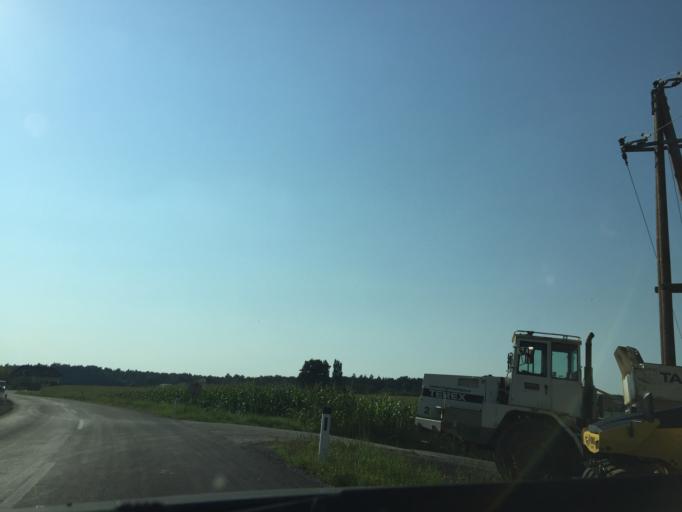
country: AT
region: Styria
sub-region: Politischer Bezirk Suedoststeiermark
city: Deutsch Goritz
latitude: 46.7415
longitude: 15.8404
